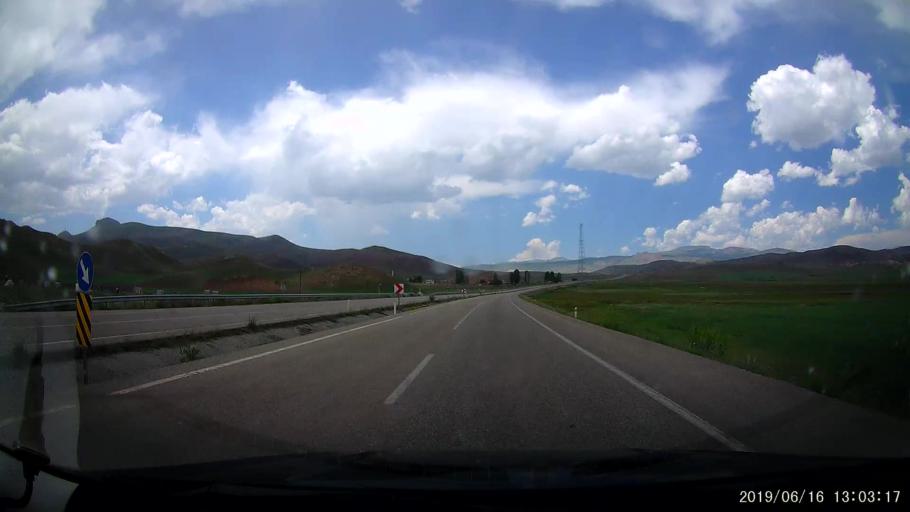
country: TR
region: Agri
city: Sulucem
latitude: 39.5798
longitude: 43.7940
